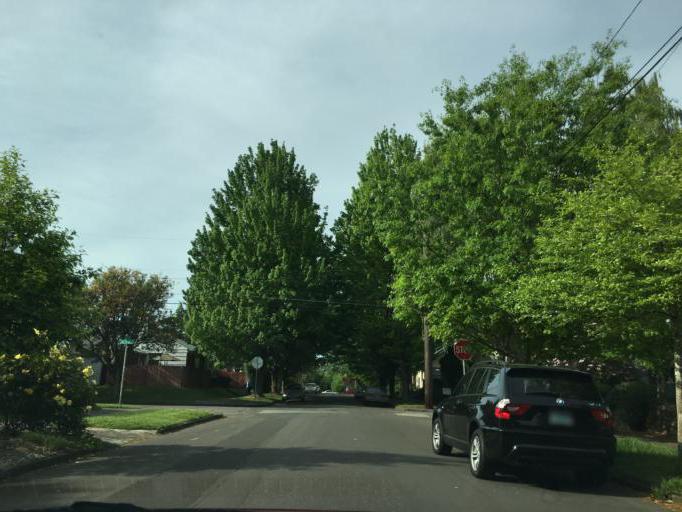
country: US
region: Oregon
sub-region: Multnomah County
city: Lents
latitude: 45.5038
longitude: -122.6162
